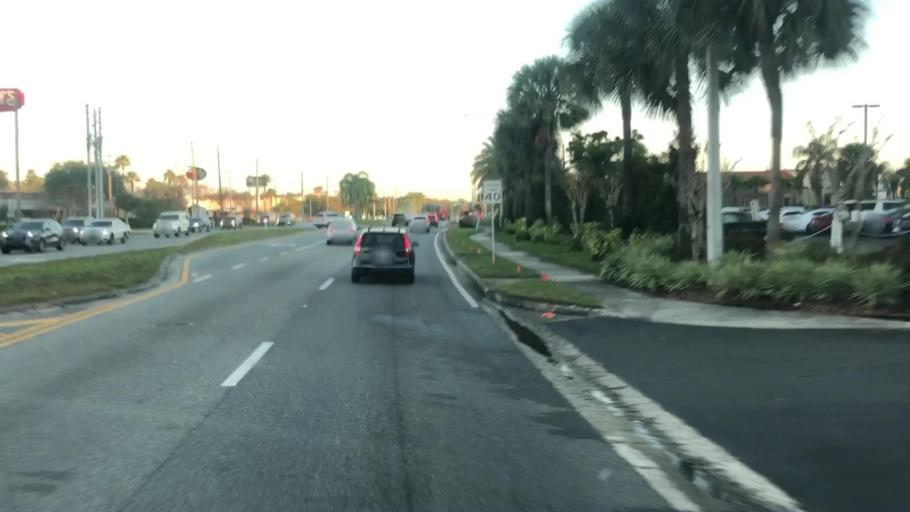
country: US
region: Florida
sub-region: Orange County
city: Doctor Phillips
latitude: 28.3867
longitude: -81.5062
